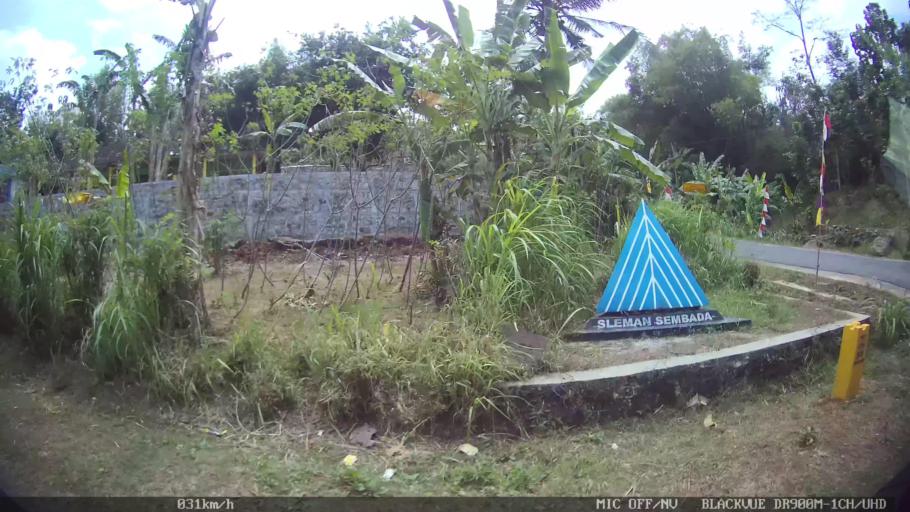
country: ID
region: Central Java
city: Candi Prambanan
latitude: -7.8201
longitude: 110.5236
